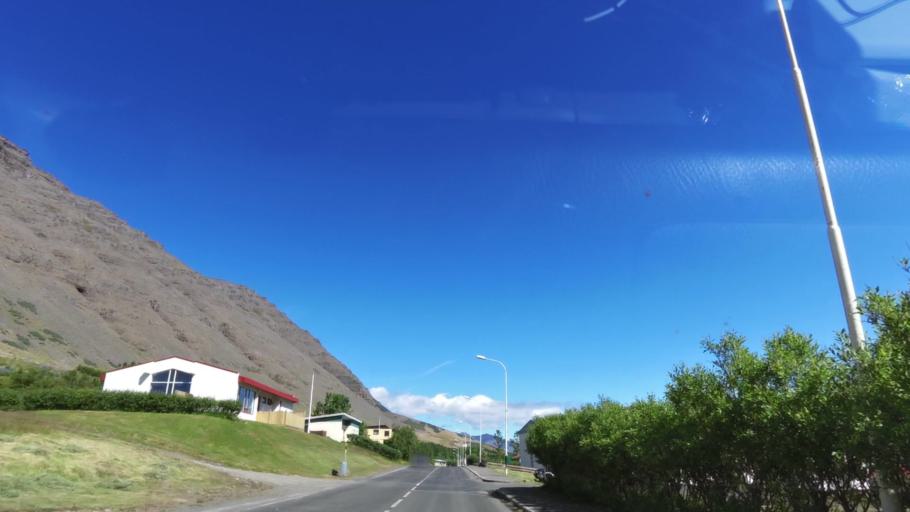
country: IS
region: Westfjords
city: Isafjoerdur
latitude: 65.6798
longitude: -23.6109
